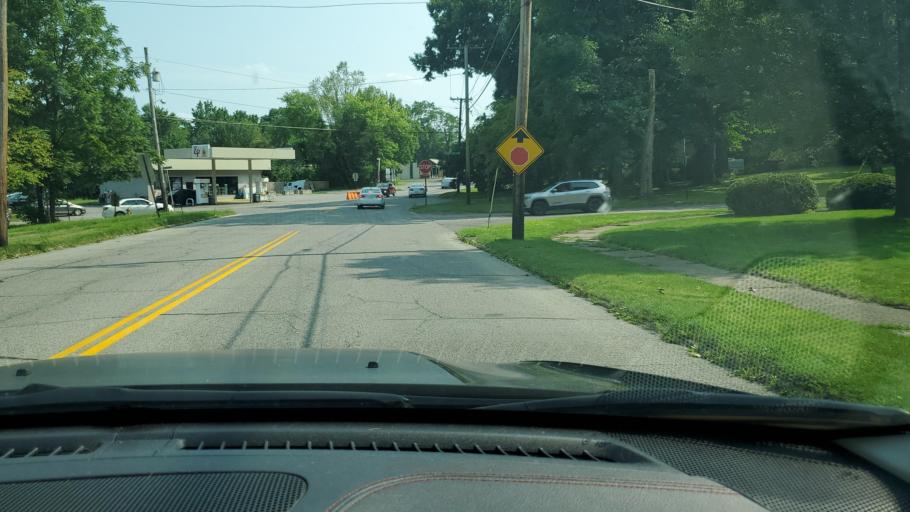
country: US
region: Ohio
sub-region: Mahoning County
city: Struthers
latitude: 41.0382
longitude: -80.6035
